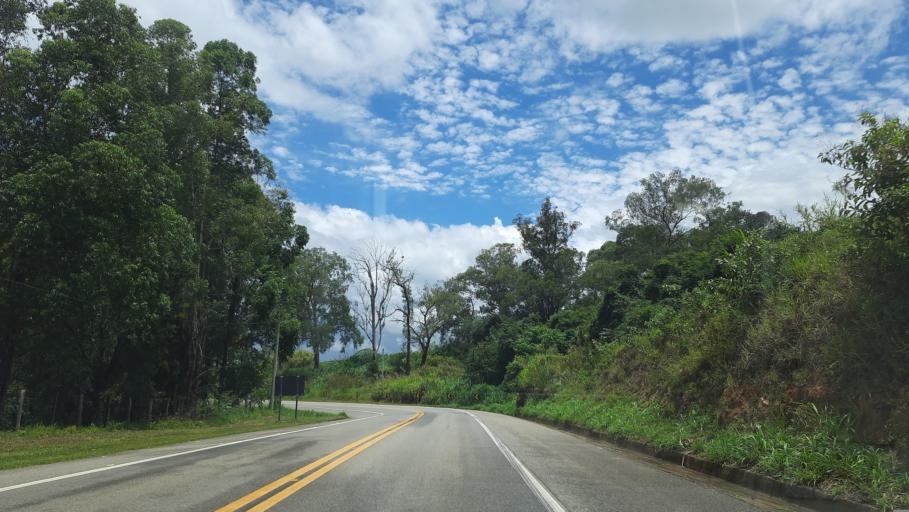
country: BR
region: Sao Paulo
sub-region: Vargem Grande Do Sul
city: Vargem Grande do Sul
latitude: -21.7997
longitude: -46.8116
